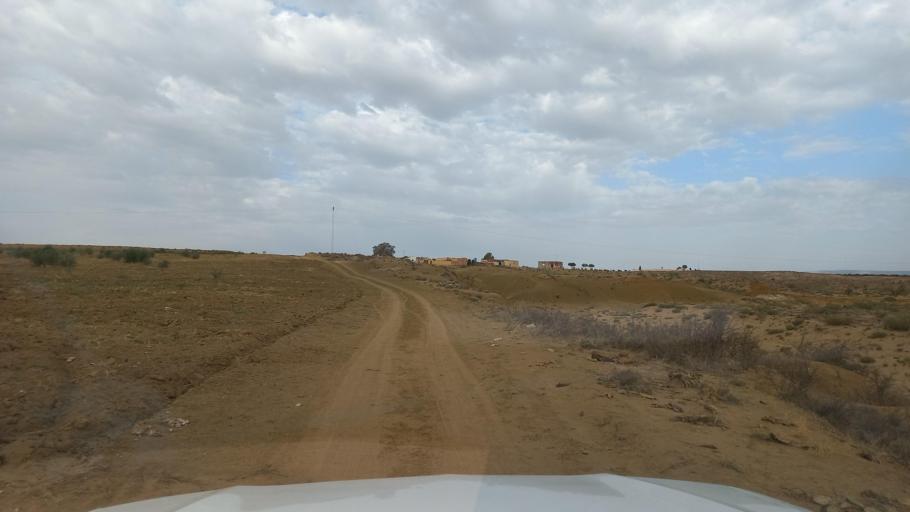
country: TN
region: Al Qasrayn
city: Kasserine
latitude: 35.2043
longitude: 9.0538
